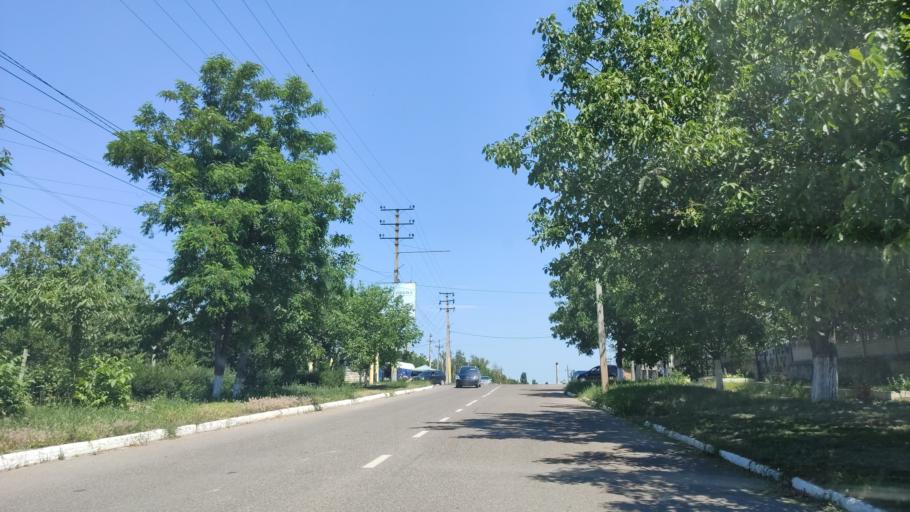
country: MD
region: Raionul Soroca
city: Soroca
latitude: 48.1511
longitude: 28.2767
